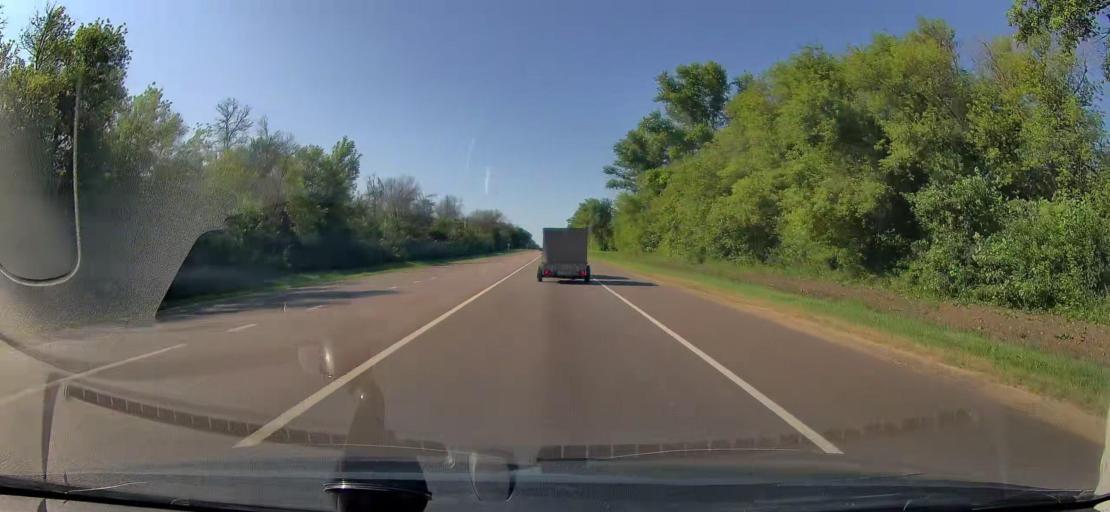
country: RU
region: Orjol
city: Kromy
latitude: 52.6071
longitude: 35.7619
